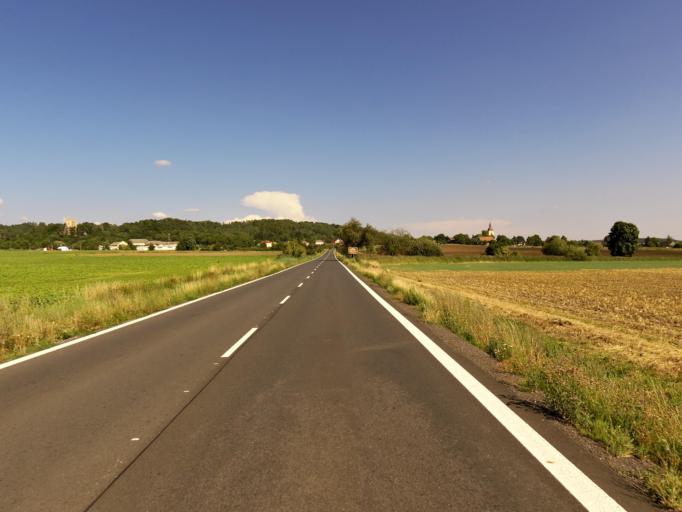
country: CZ
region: Central Bohemia
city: Knezmost
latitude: 50.5077
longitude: 15.0134
